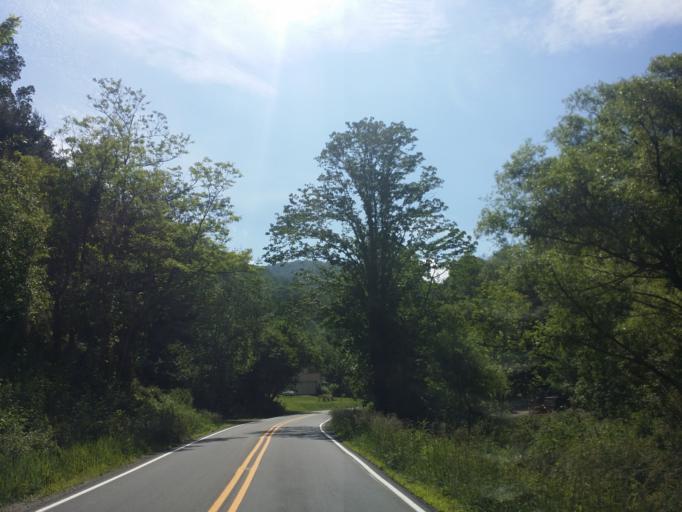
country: US
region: North Carolina
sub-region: Madison County
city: Marshall
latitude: 35.7494
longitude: -82.8653
